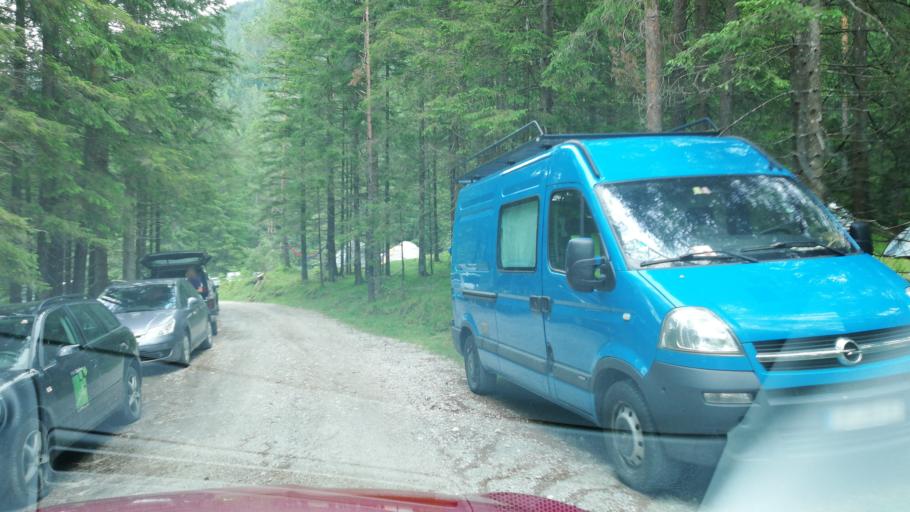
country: AT
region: Tyrol
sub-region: Politischer Bezirk Kitzbuhel
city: Waidring
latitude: 47.5445
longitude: 12.5714
